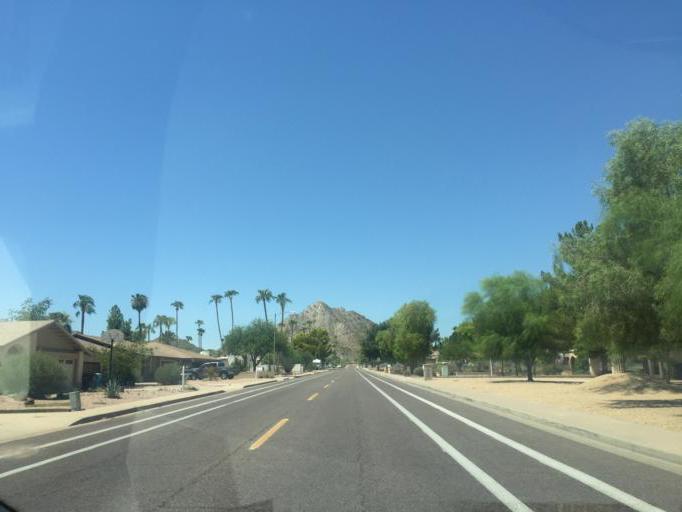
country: US
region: Arizona
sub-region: Maricopa County
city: Paradise Valley
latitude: 33.5896
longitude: -112.0253
